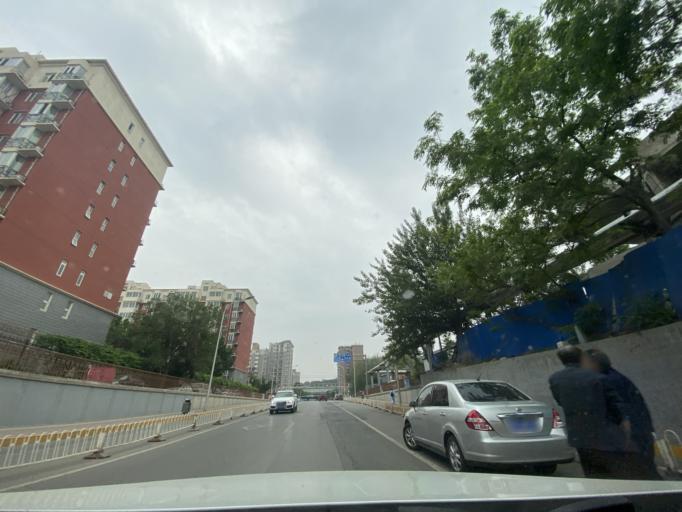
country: CN
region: Beijing
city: Sijiqing
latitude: 39.9300
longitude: 116.2421
